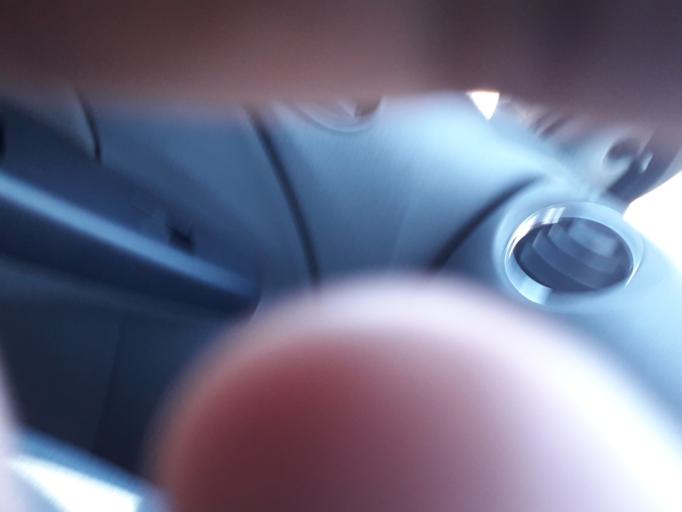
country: ZA
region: Limpopo
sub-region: Waterberg District Municipality
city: Warmbaths
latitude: -24.8247
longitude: 28.2106
